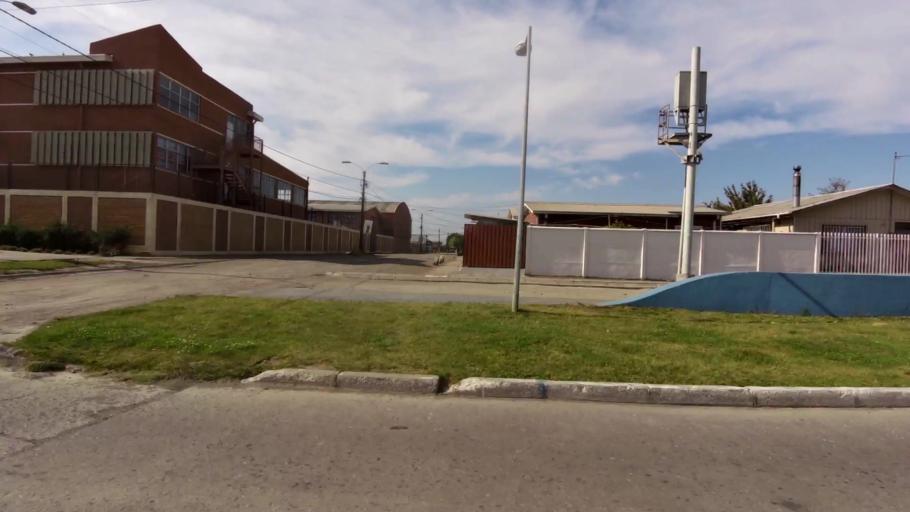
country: CL
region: Biobio
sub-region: Provincia de Concepcion
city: Talcahuano
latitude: -36.7869
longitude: -73.1110
